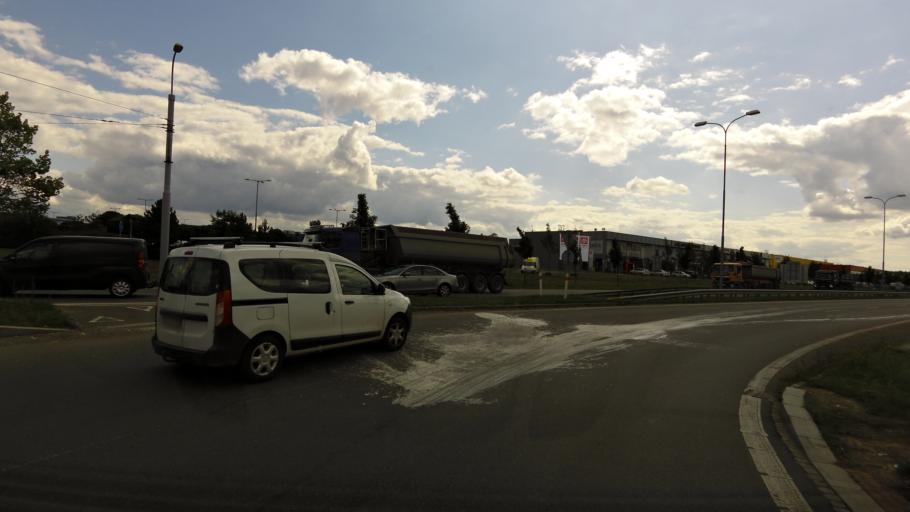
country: CZ
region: Plzensky
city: Vejprnice
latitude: 49.7309
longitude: 13.3201
